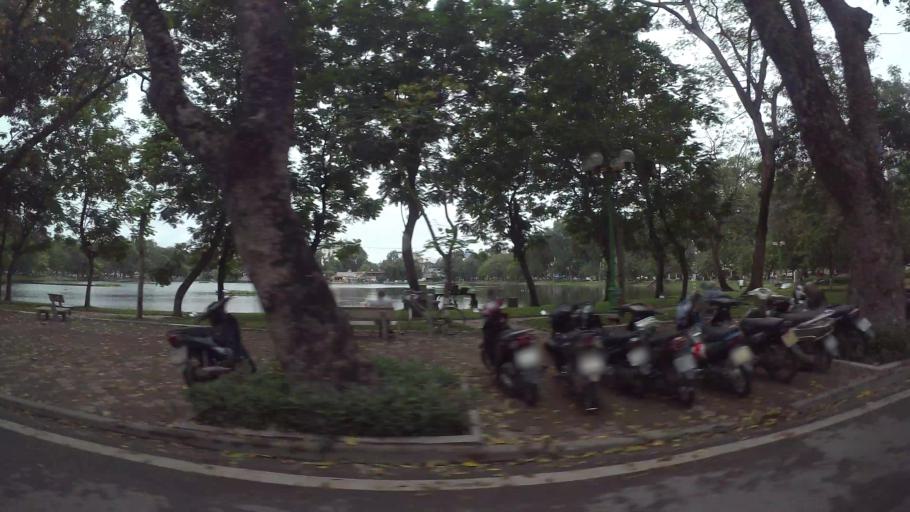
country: VN
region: Ha Noi
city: Hai BaTrung
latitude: 21.0184
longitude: 105.8474
